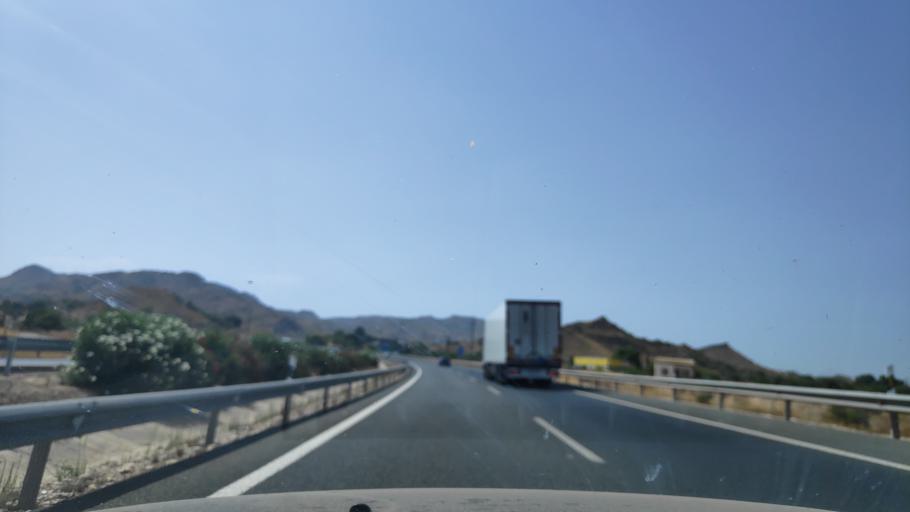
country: ES
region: Murcia
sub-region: Murcia
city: Archena
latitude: 38.1520
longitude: -1.2838
